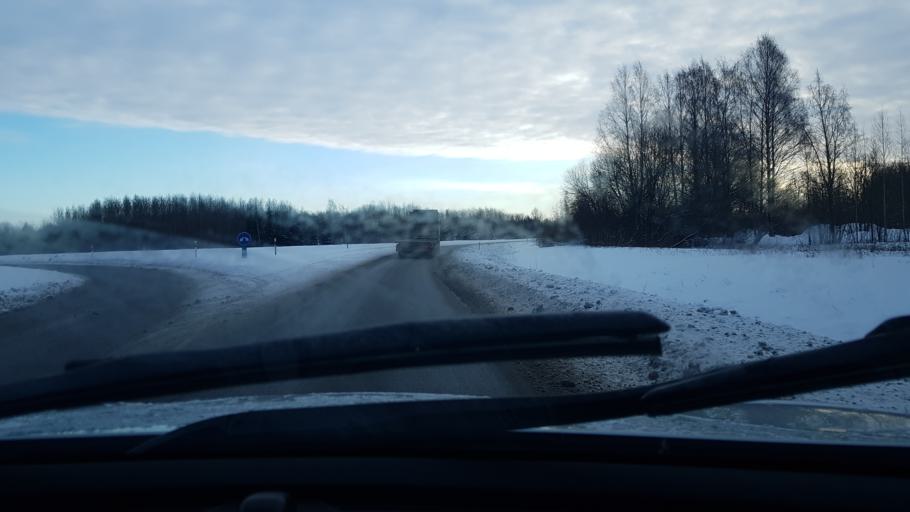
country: EE
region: Harju
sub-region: Tallinna linn
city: Kose
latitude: 59.4414
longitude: 24.9081
